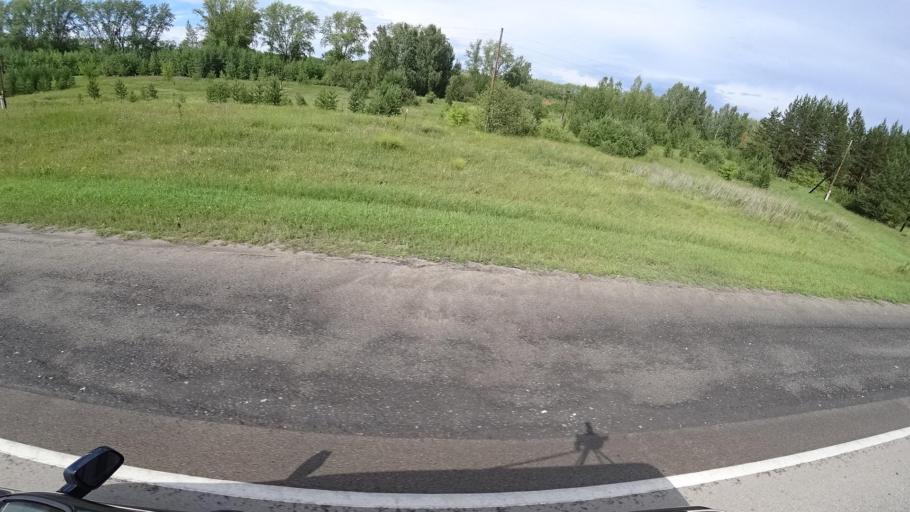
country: RU
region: Sverdlovsk
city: Kamyshlov
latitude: 56.8429
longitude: 62.7780
